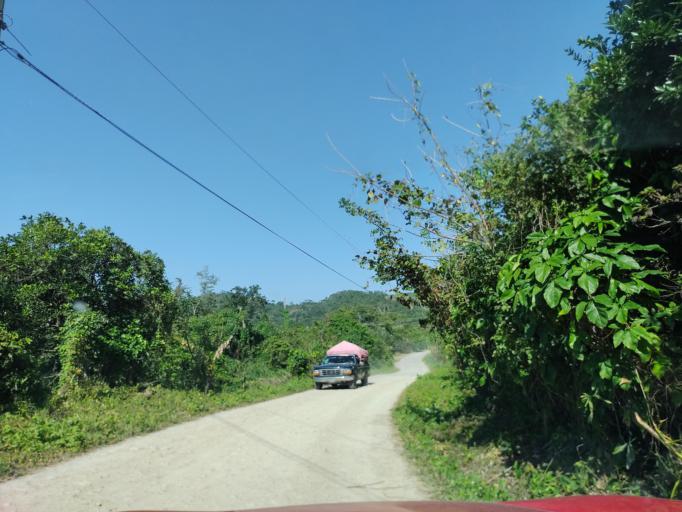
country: MX
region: Veracruz
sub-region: Papantla
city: Polutla
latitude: 20.4892
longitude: -97.1870
